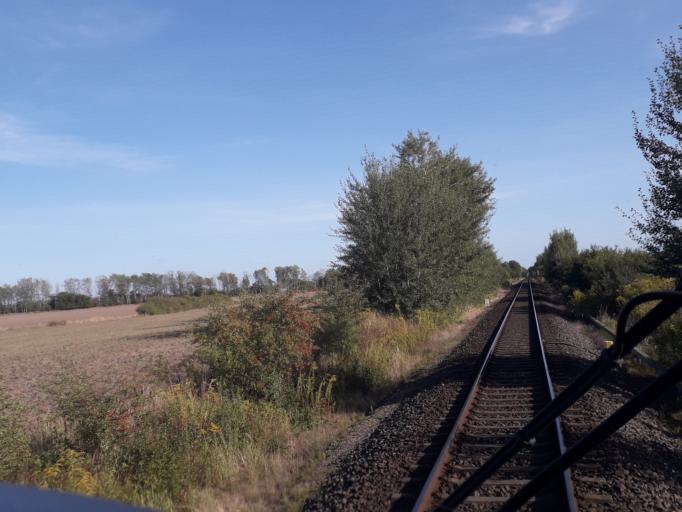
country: DE
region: Brandenburg
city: Velten
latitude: 52.6994
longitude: 13.1505
